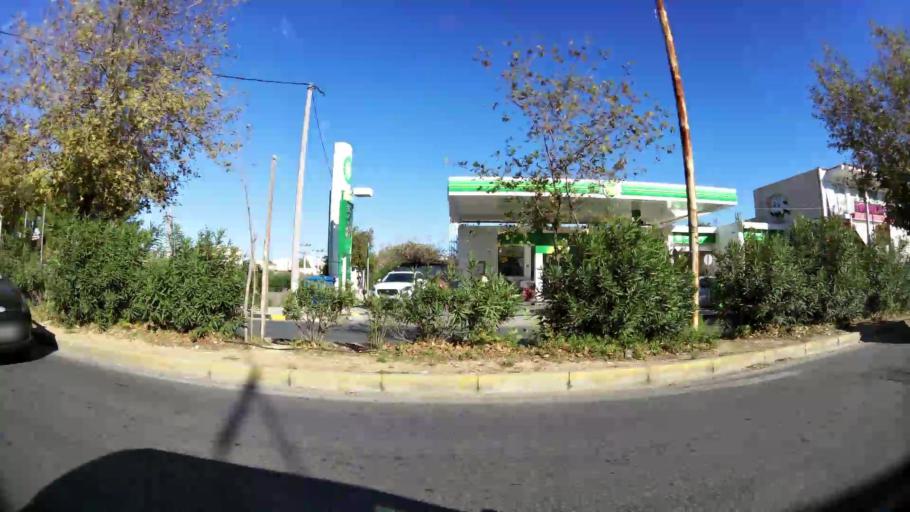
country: GR
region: Attica
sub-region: Nomarchia Anatolikis Attikis
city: Leondarion
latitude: 37.9849
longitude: 23.8509
